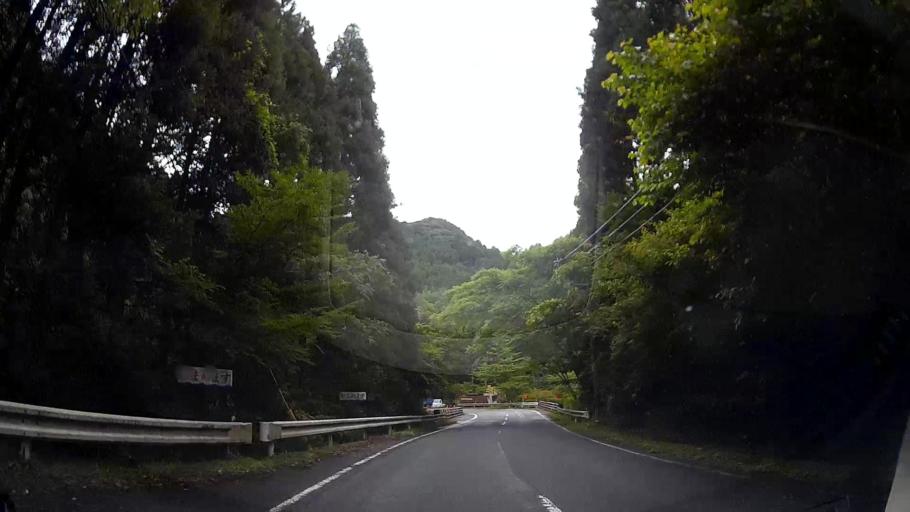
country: JP
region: Kumamoto
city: Kikuchi
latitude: 33.0735
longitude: 130.9276
